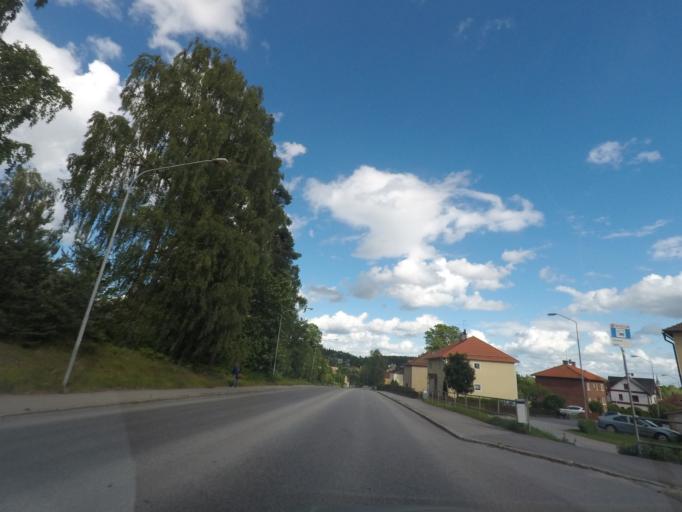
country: SE
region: OErebro
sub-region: Lindesbergs Kommun
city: Lindesberg
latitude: 59.6005
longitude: 15.2165
